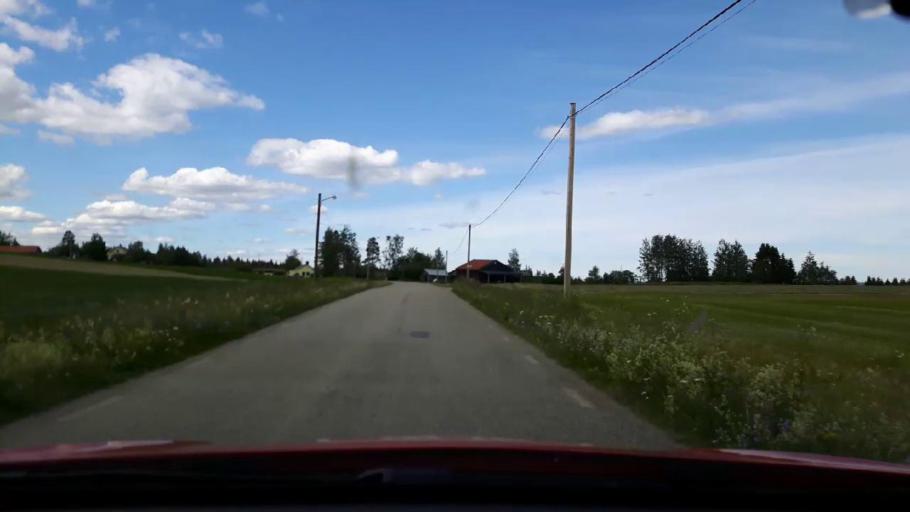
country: SE
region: Jaemtland
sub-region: Bergs Kommun
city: Hoverberg
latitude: 62.8304
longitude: 14.4583
